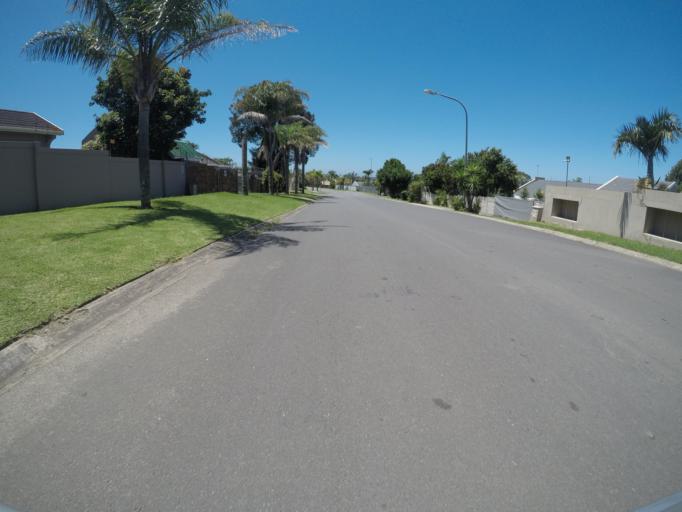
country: ZA
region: Eastern Cape
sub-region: Buffalo City Metropolitan Municipality
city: East London
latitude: -32.9547
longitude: 27.9359
